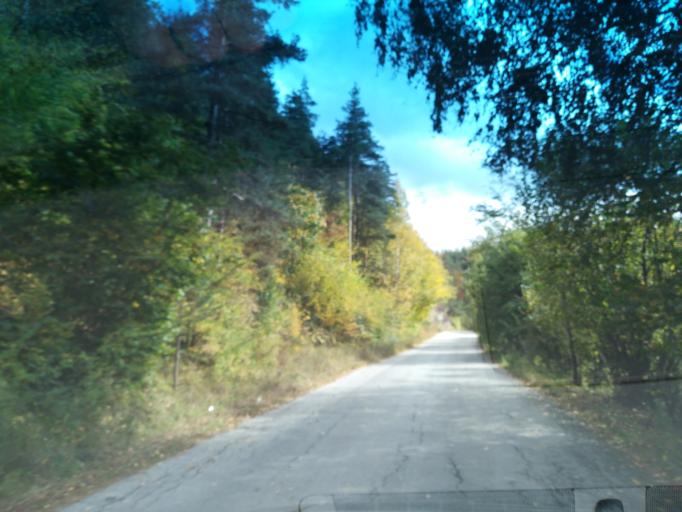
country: BG
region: Pazardzhik
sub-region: Obshtina Batak
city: Batak
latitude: 41.9555
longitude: 24.2400
